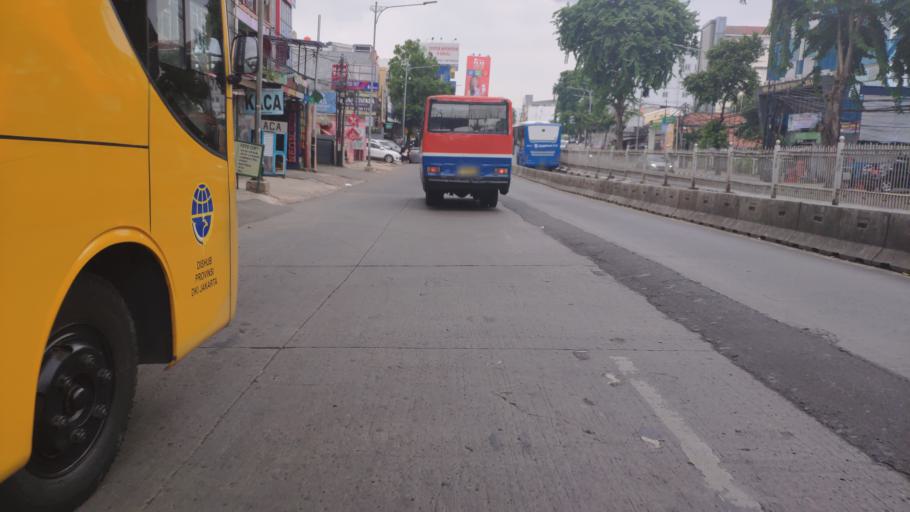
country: ID
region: Jakarta Raya
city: Jakarta
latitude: -6.2739
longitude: 106.8303
